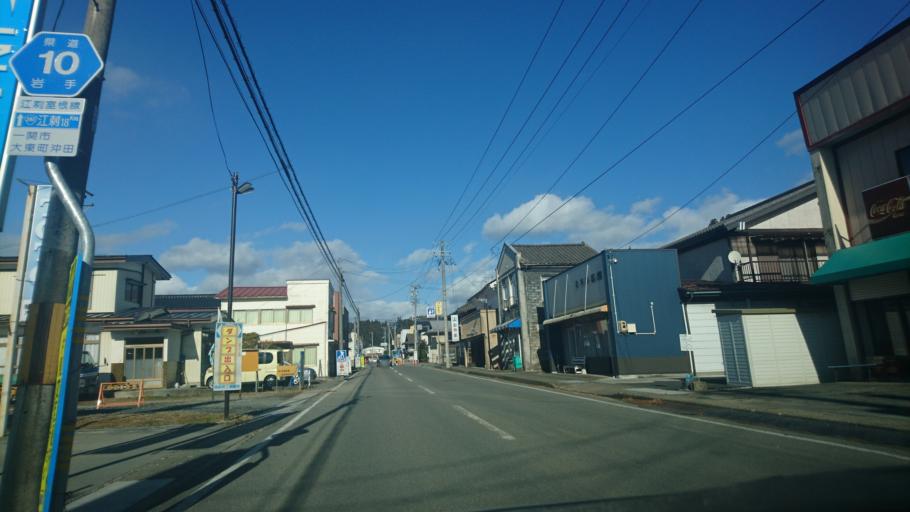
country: JP
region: Iwate
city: Mizusawa
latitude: 39.0467
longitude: 141.3668
